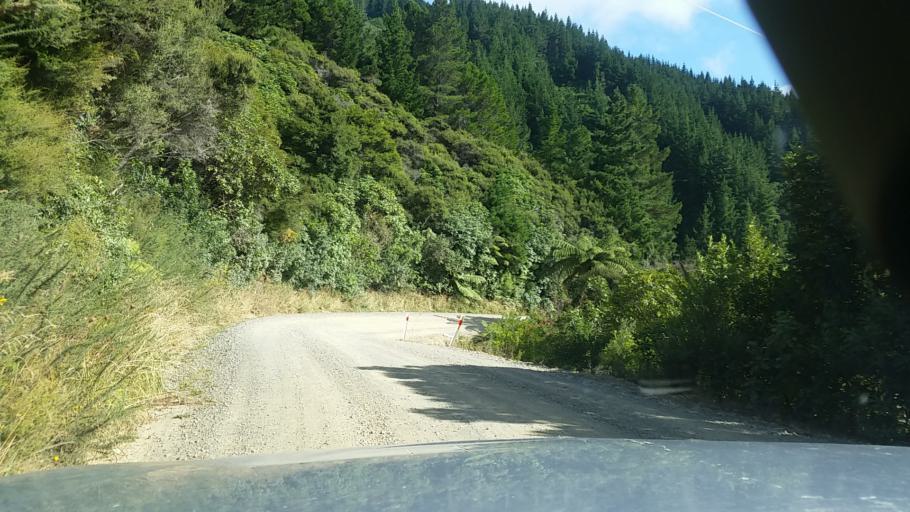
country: NZ
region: Marlborough
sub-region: Marlborough District
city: Picton
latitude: -41.2915
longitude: 174.1297
